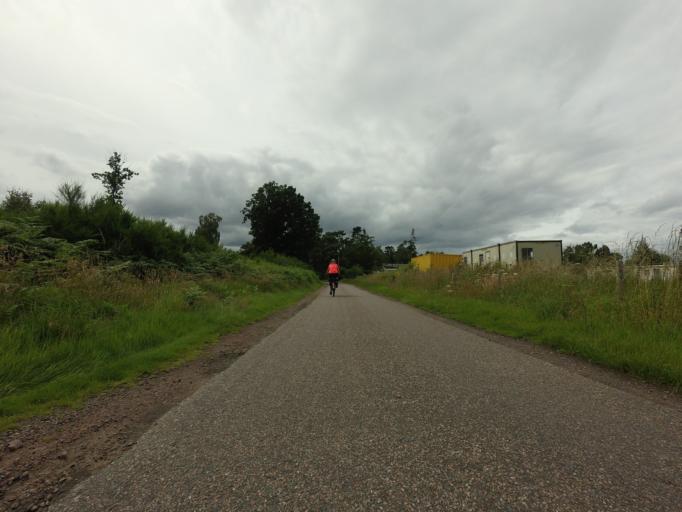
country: GB
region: Scotland
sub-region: Moray
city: Forres
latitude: 57.6051
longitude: -3.7512
